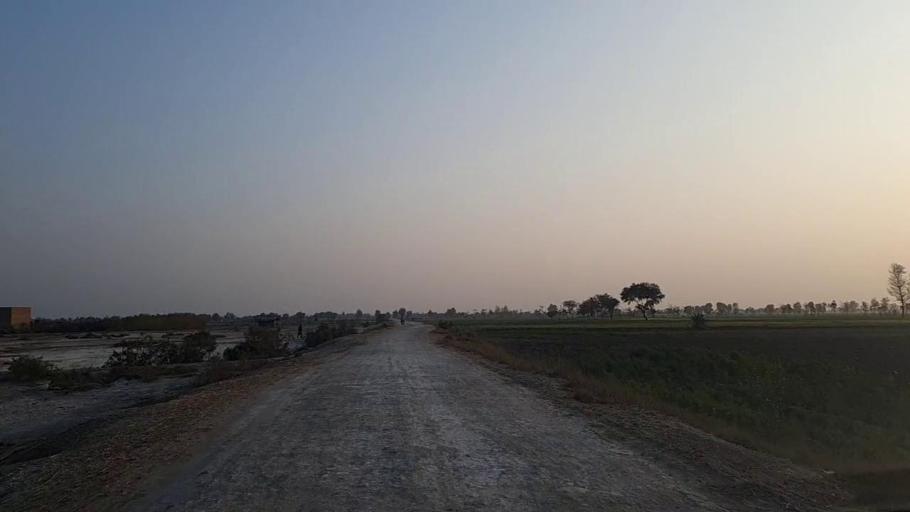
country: PK
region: Sindh
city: Daur
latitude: 26.4252
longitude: 68.3679
